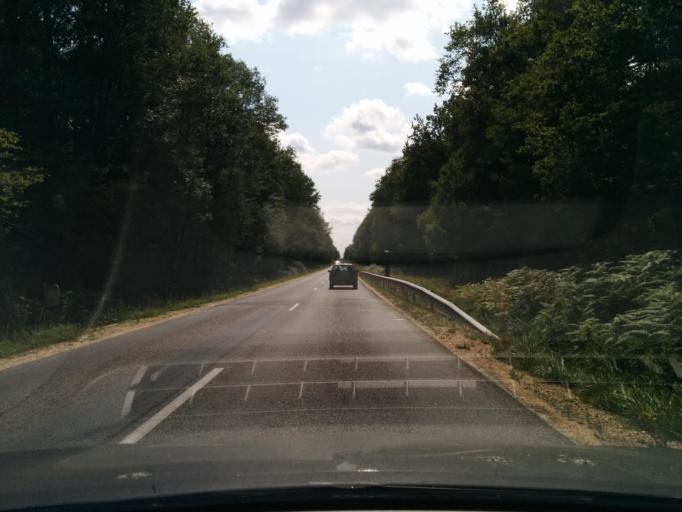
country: FR
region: Centre
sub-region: Departement du Cher
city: Neuvy-sur-Barangeon
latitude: 47.2841
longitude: 2.1911
